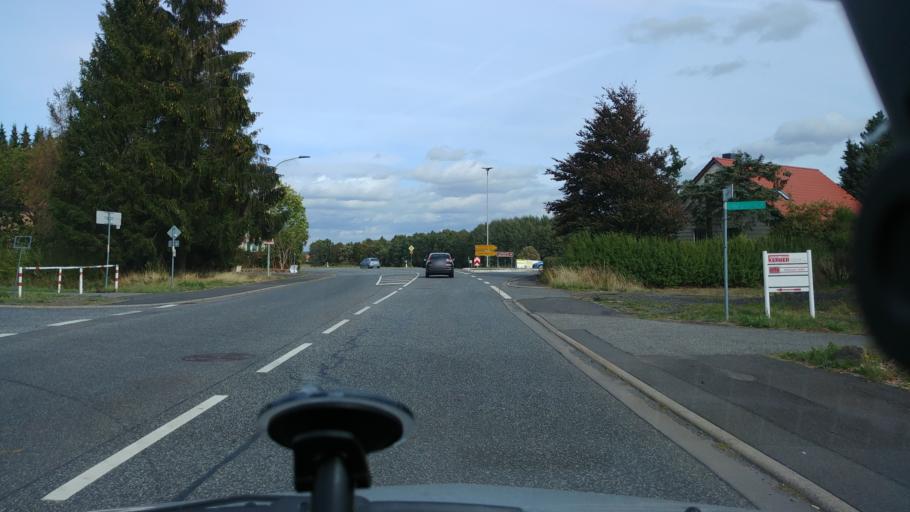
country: DE
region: Hesse
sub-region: Regierungsbezirk Giessen
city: Grebenhain
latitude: 50.4942
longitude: 9.3482
